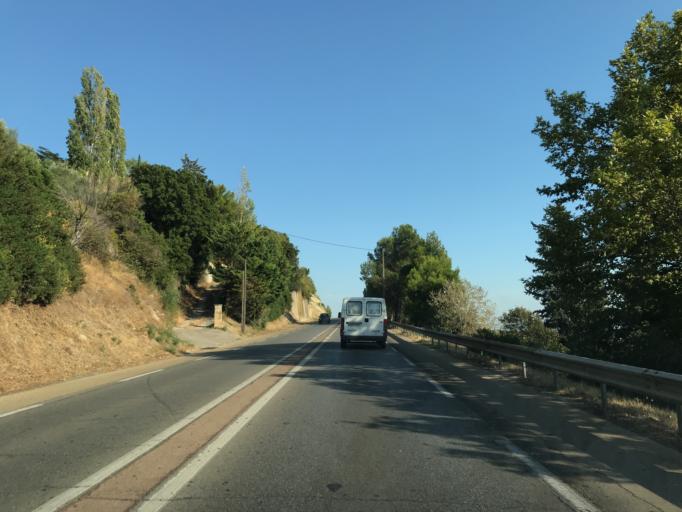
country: FR
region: Provence-Alpes-Cote d'Azur
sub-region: Departement des Bouches-du-Rhone
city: Saint-Chamas
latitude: 43.5537
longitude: 5.0346
